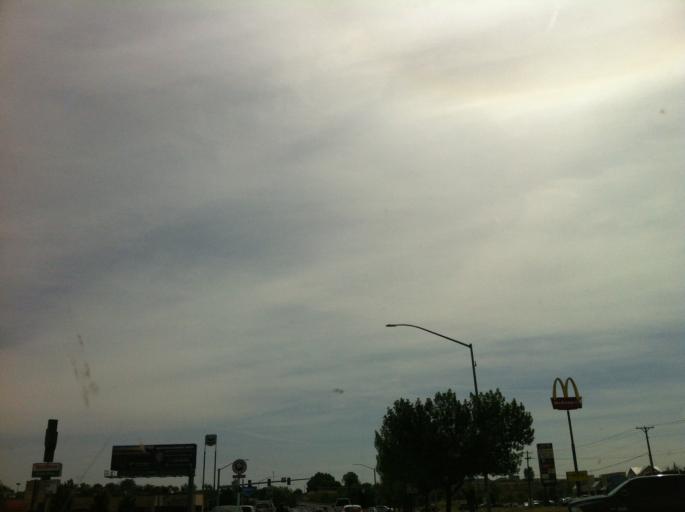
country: US
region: Oregon
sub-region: Malheur County
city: Ontario
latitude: 44.0247
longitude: -116.9443
